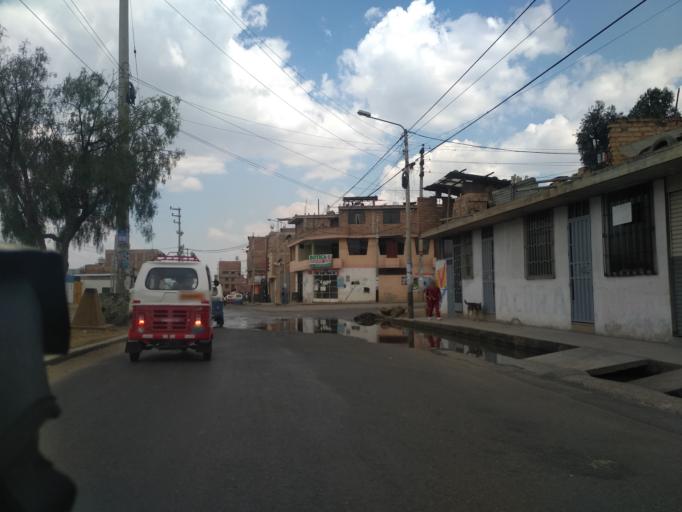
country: PE
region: Cajamarca
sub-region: Provincia de Cajamarca
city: Cajamarca
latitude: -7.1746
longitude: -78.4919
